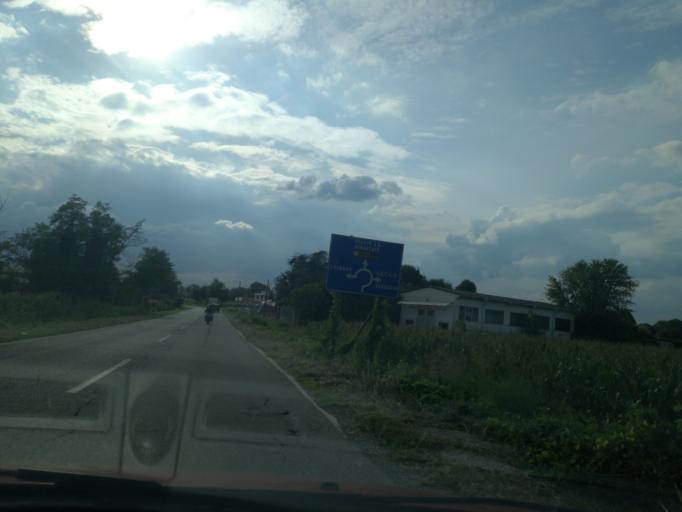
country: IT
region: Lombardy
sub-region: Provincia di Monza e Brianza
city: Cornate d'Adda
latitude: 45.6397
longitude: 9.4733
